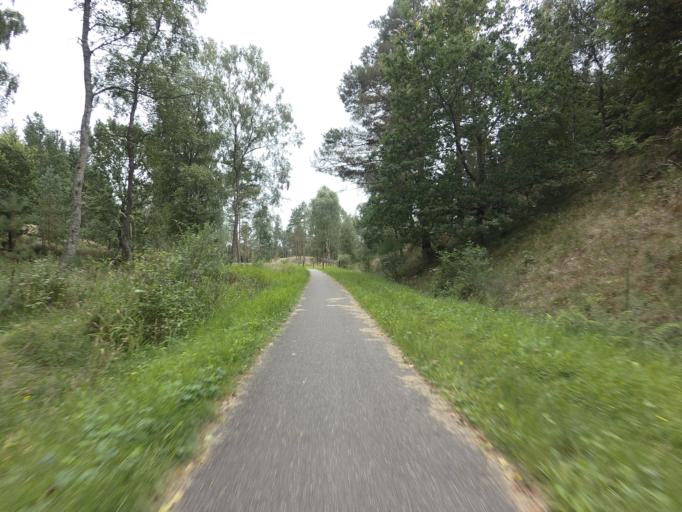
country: DK
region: Central Jutland
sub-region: Silkeborg Kommune
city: Virklund
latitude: 56.0576
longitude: 9.4712
